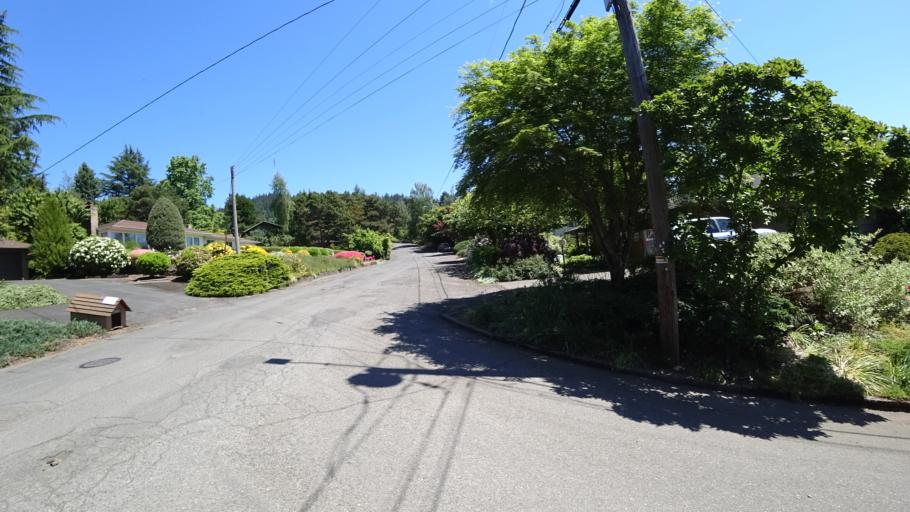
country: US
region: Oregon
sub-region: Washington County
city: Raleigh Hills
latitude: 45.4941
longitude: -122.7182
